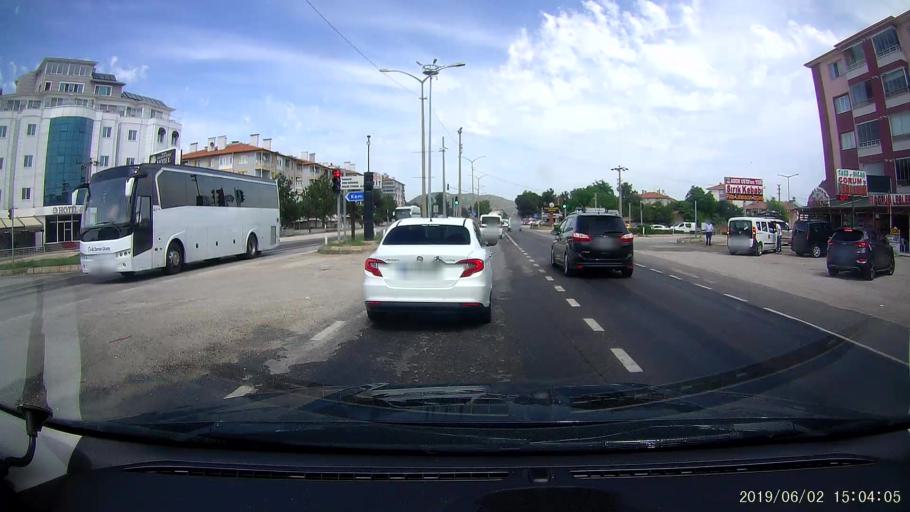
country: TR
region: Corum
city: Osmancik
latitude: 40.9790
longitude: 34.7904
